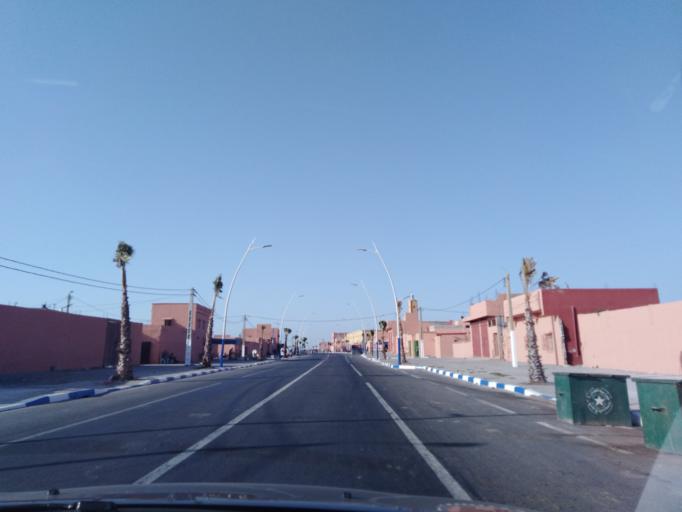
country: MA
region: Doukkala-Abda
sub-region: El-Jadida
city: Sidi Bennour
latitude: 32.5818
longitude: -8.7134
